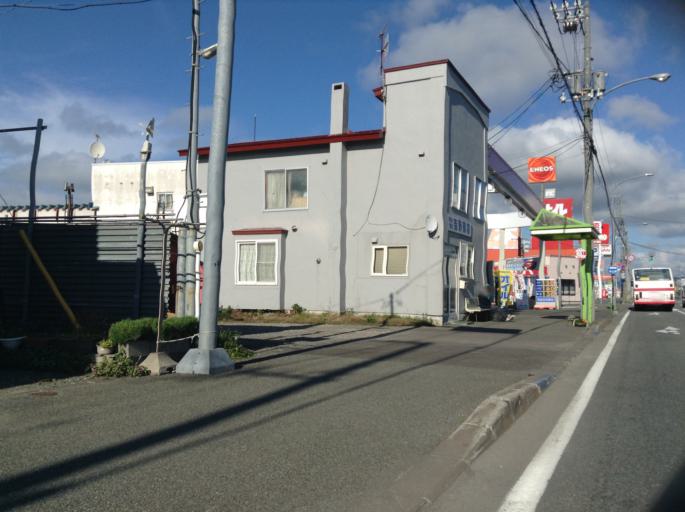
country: JP
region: Hokkaido
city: Wakkanai
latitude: 45.3962
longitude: 141.6980
